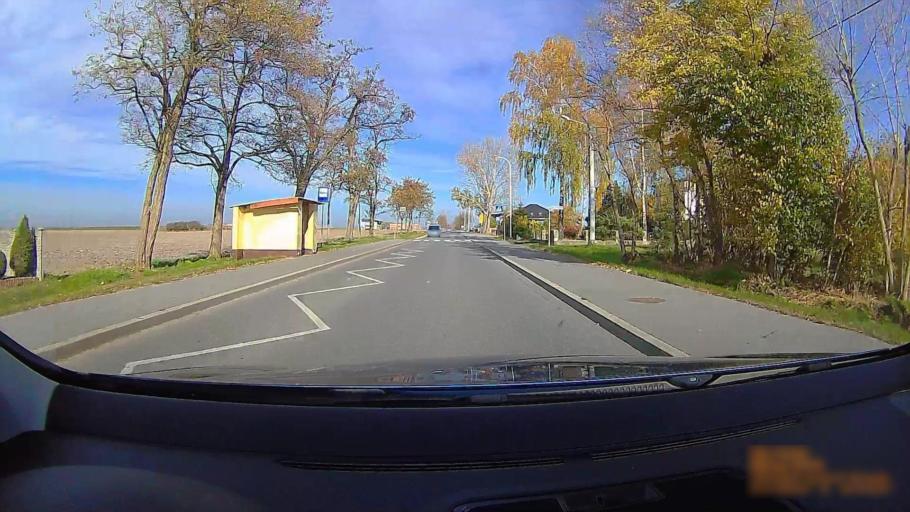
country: PL
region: Greater Poland Voivodeship
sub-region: Powiat kepinski
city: Kepno
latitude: 51.3336
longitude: 18.0192
